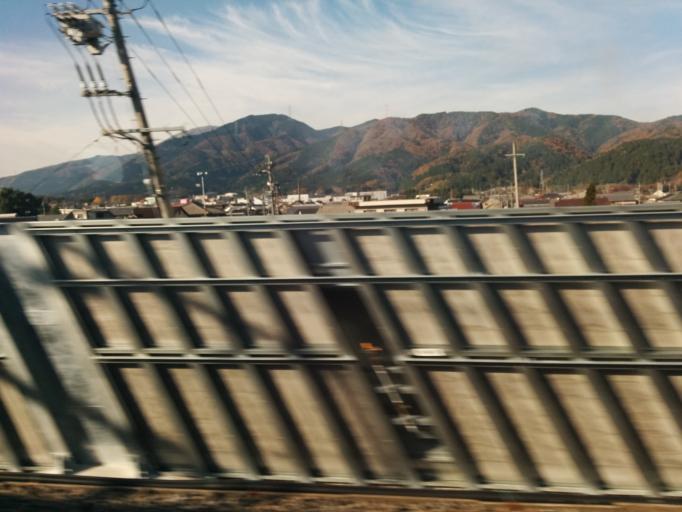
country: JP
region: Gifu
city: Tarui
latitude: 35.3595
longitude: 136.4759
